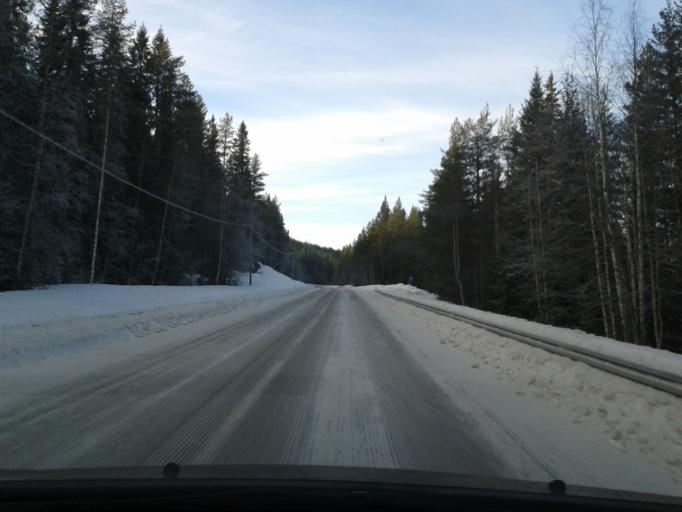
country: SE
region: Vaesternorrland
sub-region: OErnskoeldsviks Kommun
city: Bredbyn
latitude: 63.6617
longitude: 17.8474
